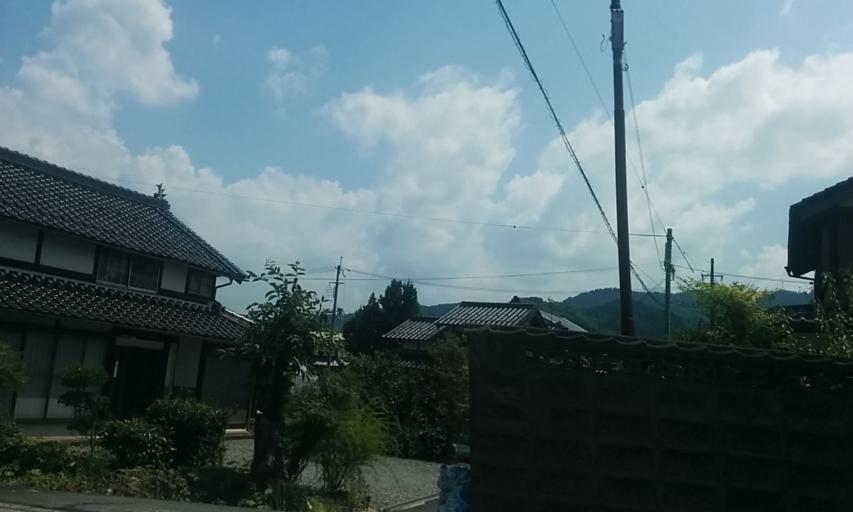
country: JP
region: Kyoto
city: Fukuchiyama
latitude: 35.2494
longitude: 135.1428
